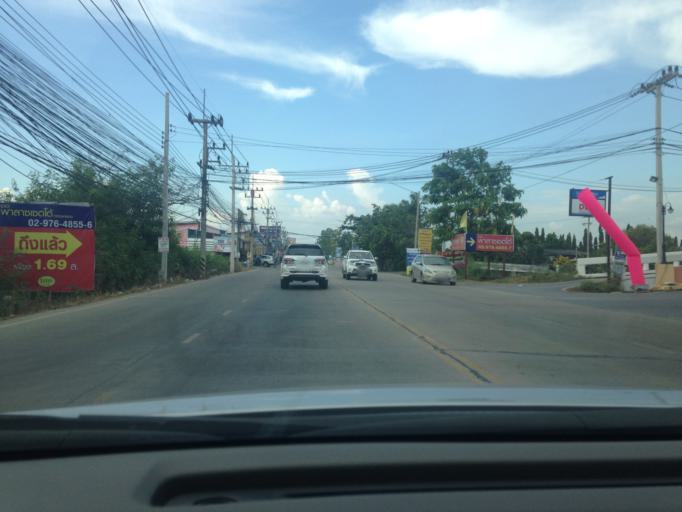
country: TH
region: Pathum Thani
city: Khlong Luang
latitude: 14.0566
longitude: 100.6635
